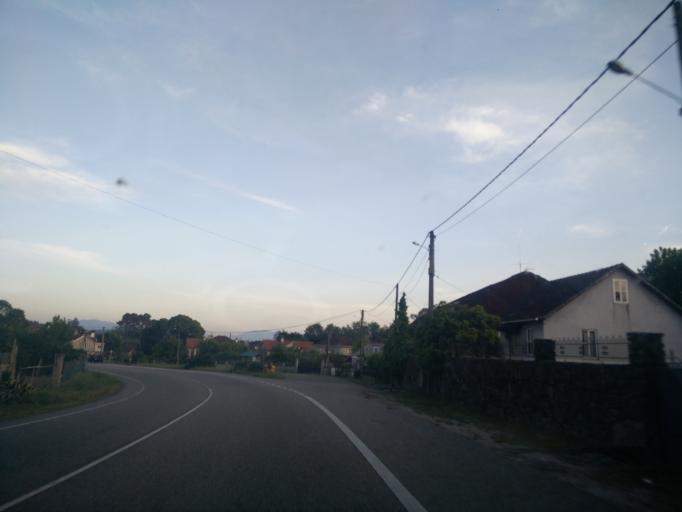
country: ES
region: Galicia
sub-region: Provincia de Pontevedra
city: Ponteareas
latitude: 42.1943
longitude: -8.5095
